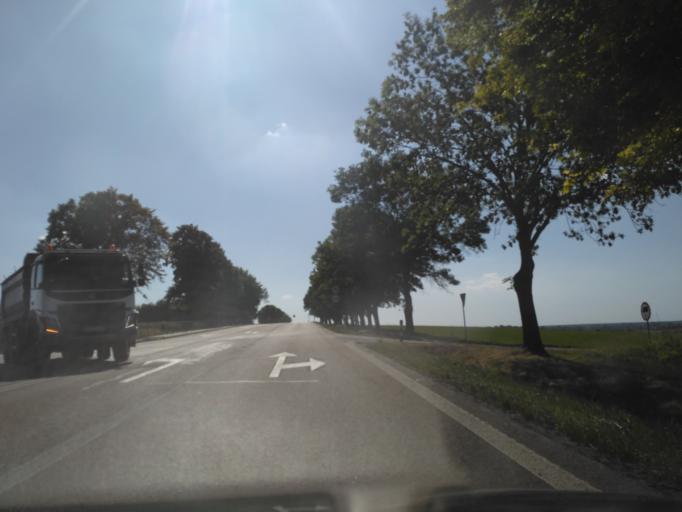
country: PL
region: Lublin Voivodeship
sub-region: Powiat swidnicki
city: Trawniki
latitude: 51.1704
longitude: 23.1120
